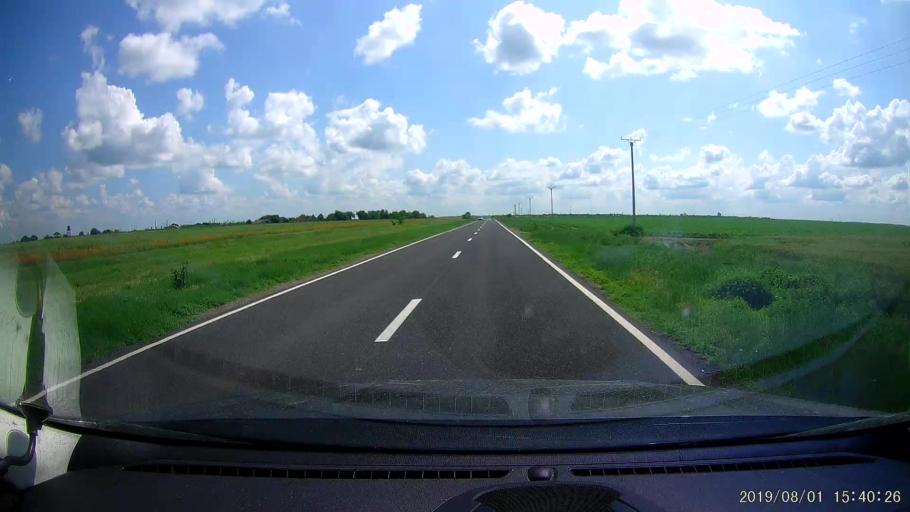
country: RO
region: Braila
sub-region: Comuna Baraganul
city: Baraganul
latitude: 44.8375
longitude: 27.5426
